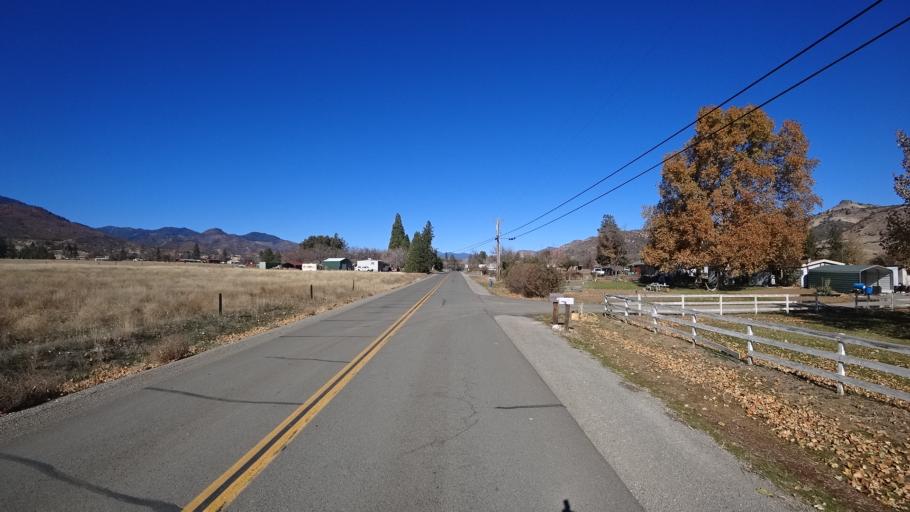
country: US
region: California
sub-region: Siskiyou County
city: Montague
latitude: 41.9064
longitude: -122.5563
